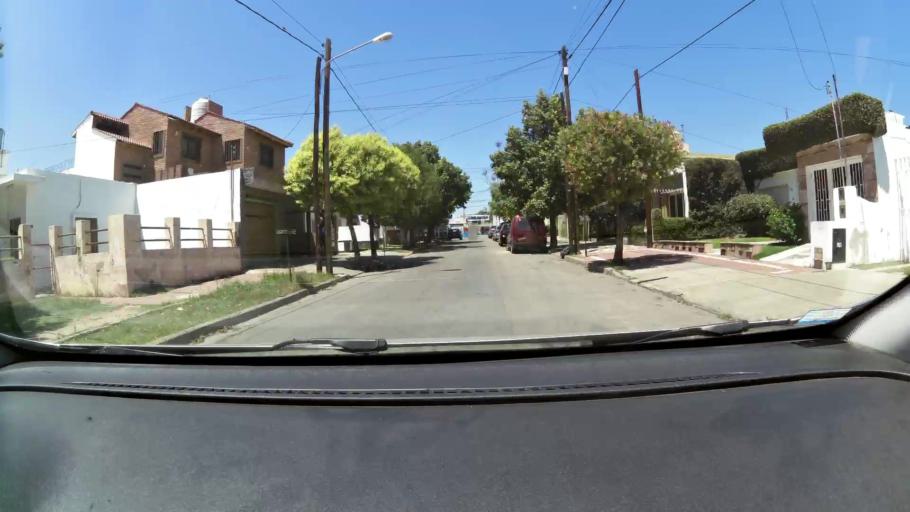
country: AR
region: Cordoba
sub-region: Departamento de Capital
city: Cordoba
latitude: -31.4145
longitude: -64.2178
